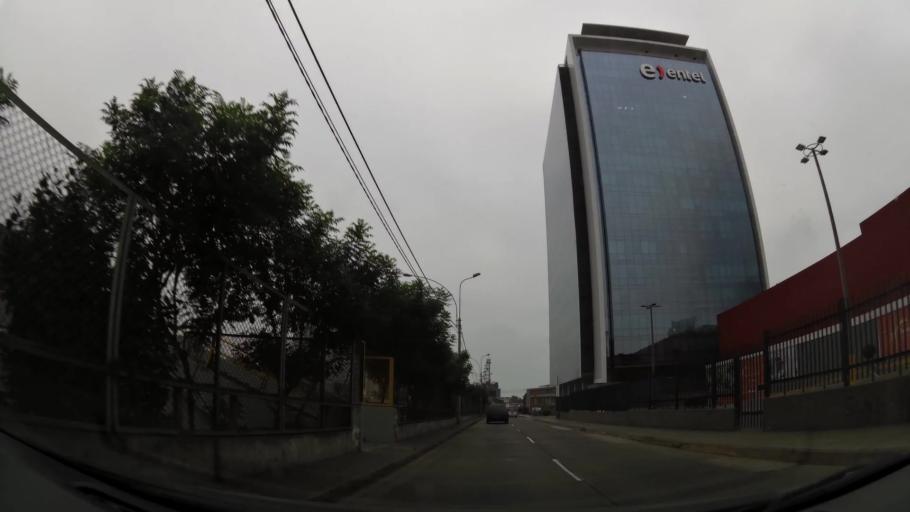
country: PE
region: Lima
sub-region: Lima
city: San Isidro
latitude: -12.0976
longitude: -77.0258
